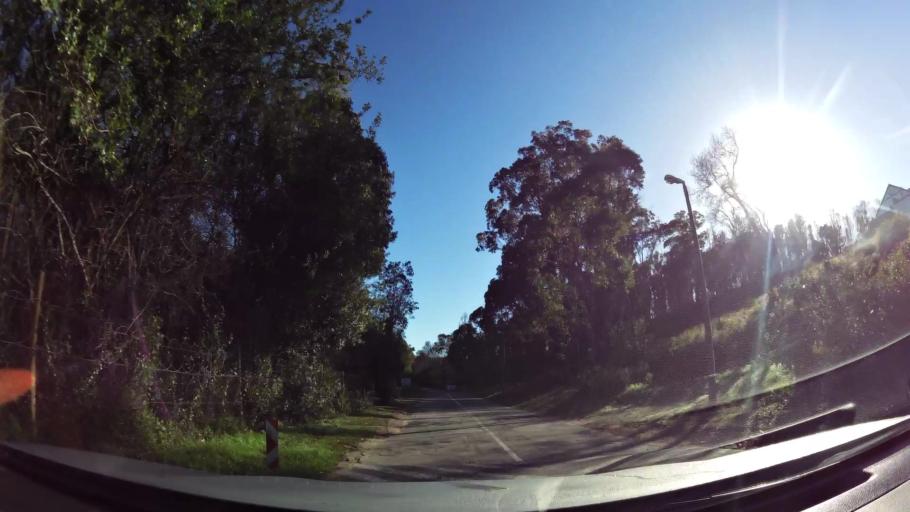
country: ZA
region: Western Cape
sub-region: Eden District Municipality
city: Knysna
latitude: -34.0330
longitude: 23.0147
